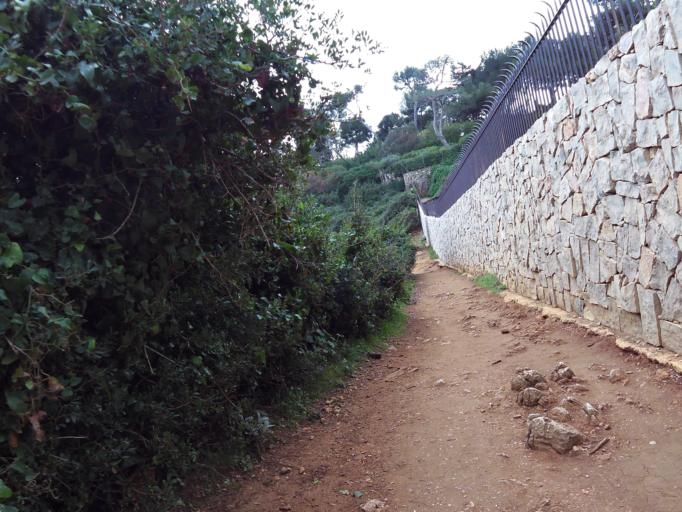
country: FR
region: Provence-Alpes-Cote d'Azur
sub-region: Departement des Alpes-Maritimes
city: Antibes
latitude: 43.5537
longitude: 7.1425
